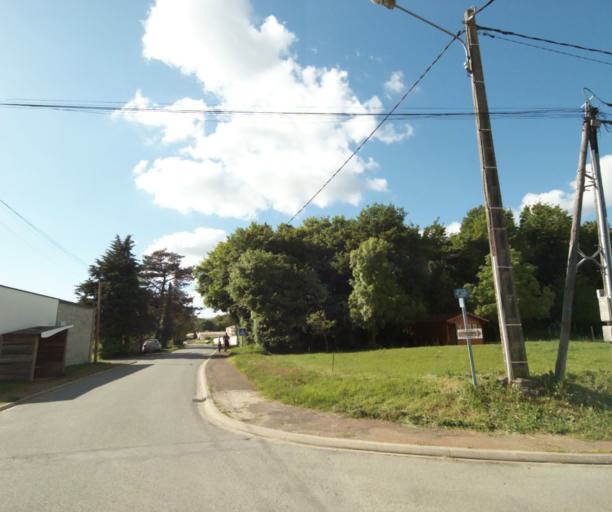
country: FR
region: Poitou-Charentes
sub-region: Departement de la Charente-Maritime
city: Nieul-les-Saintes
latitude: 45.7073
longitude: -0.7474
